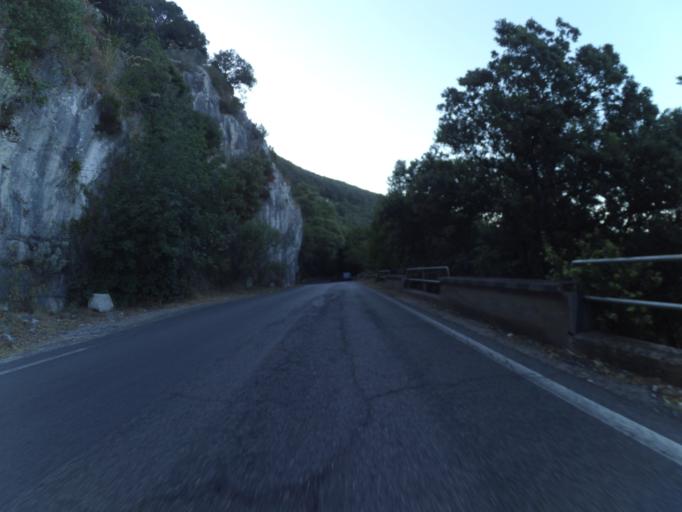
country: IT
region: Latium
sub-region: Provincia di Latina
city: San Felice Circeo
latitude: 41.2276
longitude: 13.0889
